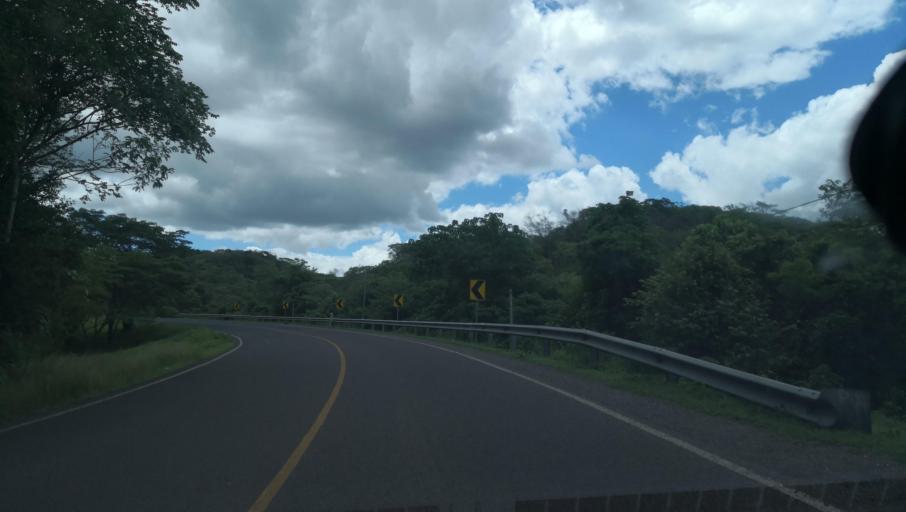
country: NI
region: Madriz
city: Palacaguina
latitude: 13.4425
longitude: -86.4371
